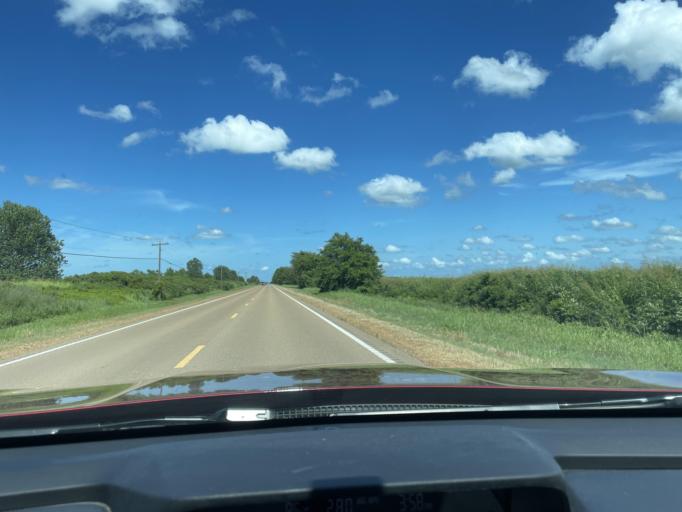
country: US
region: Mississippi
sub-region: Humphreys County
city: Belzoni
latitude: 33.1837
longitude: -90.5893
